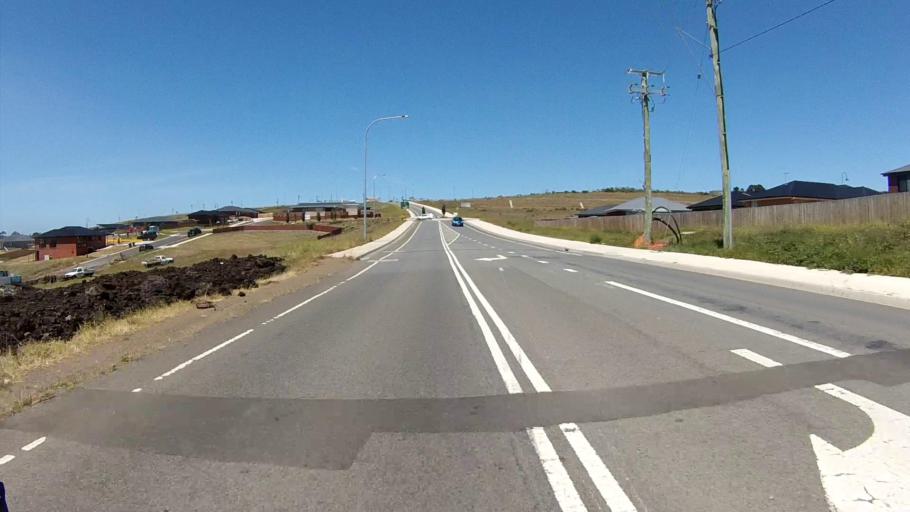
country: AU
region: Tasmania
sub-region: Clarence
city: Howrah
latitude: -42.8852
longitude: 147.4285
